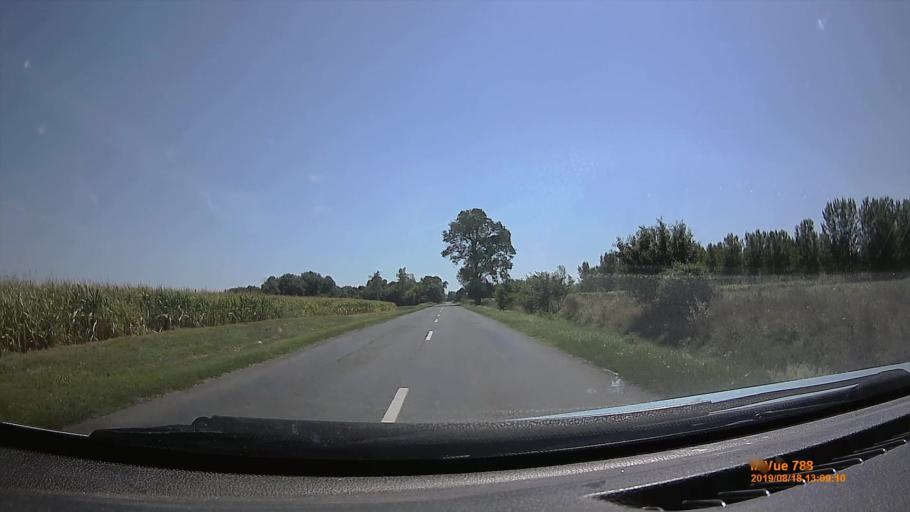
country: HU
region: Fejer
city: Kaloz
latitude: 46.9300
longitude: 18.5084
